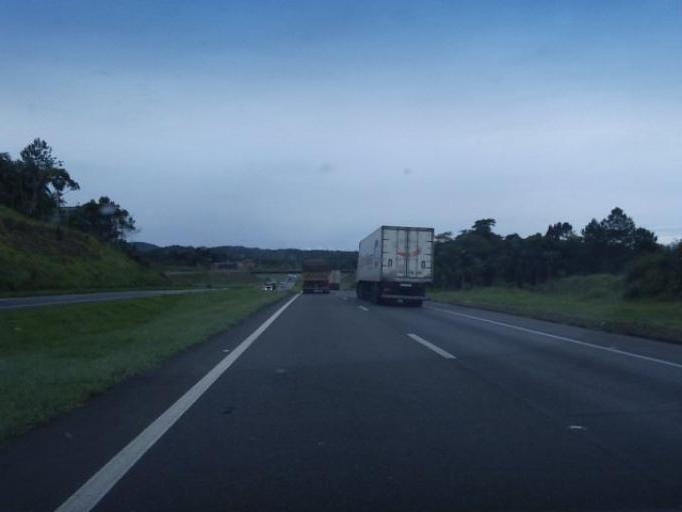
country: BR
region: Sao Paulo
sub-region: Pariquera-Acu
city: Pariquera Acu
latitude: -24.6410
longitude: -47.9152
